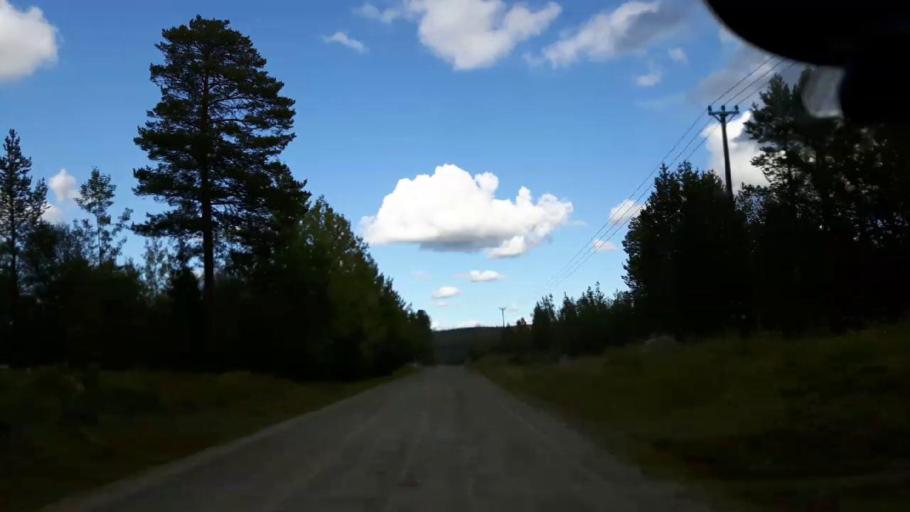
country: SE
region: Jaemtland
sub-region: Stroemsunds Kommun
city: Stroemsund
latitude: 63.4176
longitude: 15.7926
